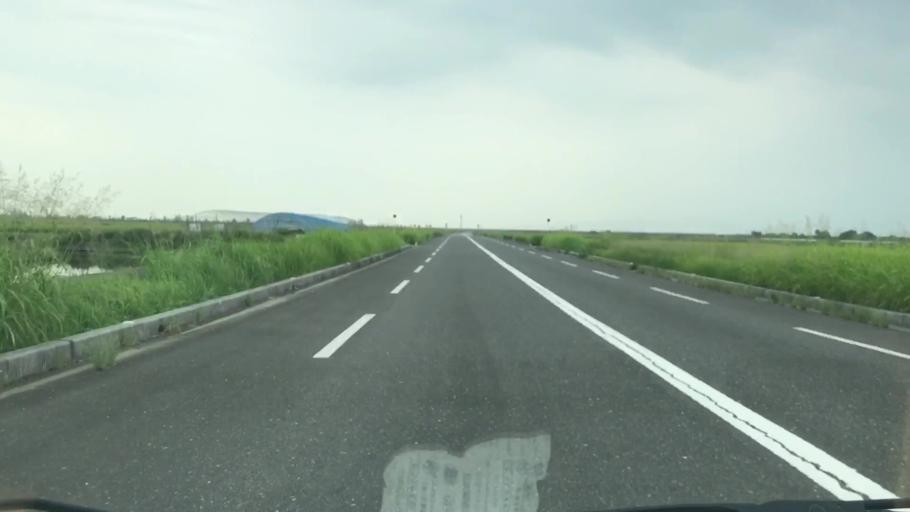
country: JP
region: Saga Prefecture
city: Okawa
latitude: 33.1714
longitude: 130.2949
